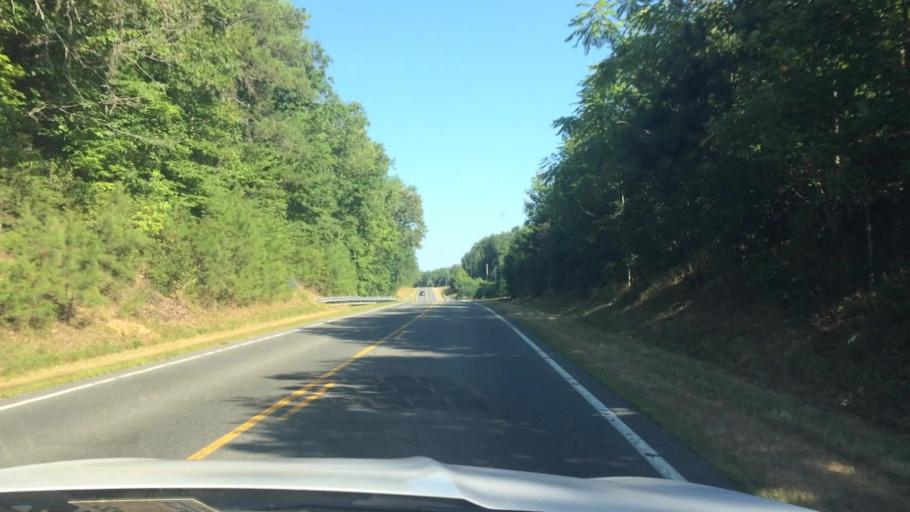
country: US
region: Virginia
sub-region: Lancaster County
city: Lancaster
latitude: 37.8188
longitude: -76.5520
